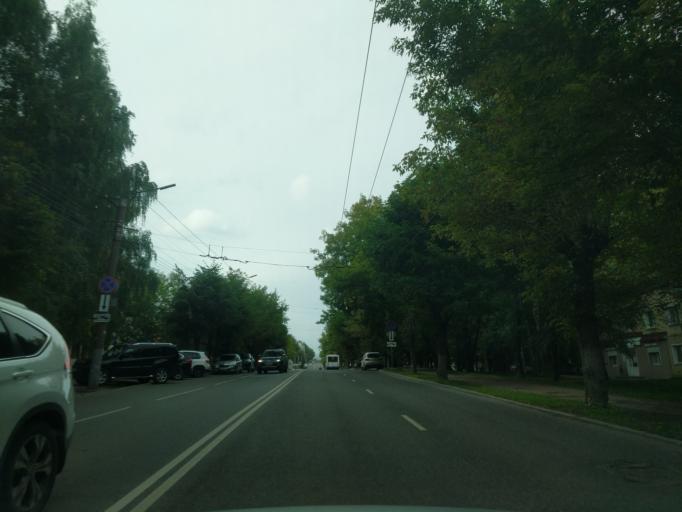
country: RU
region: Kirov
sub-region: Kirovo-Chepetskiy Rayon
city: Kirov
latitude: 58.5875
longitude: 49.6695
